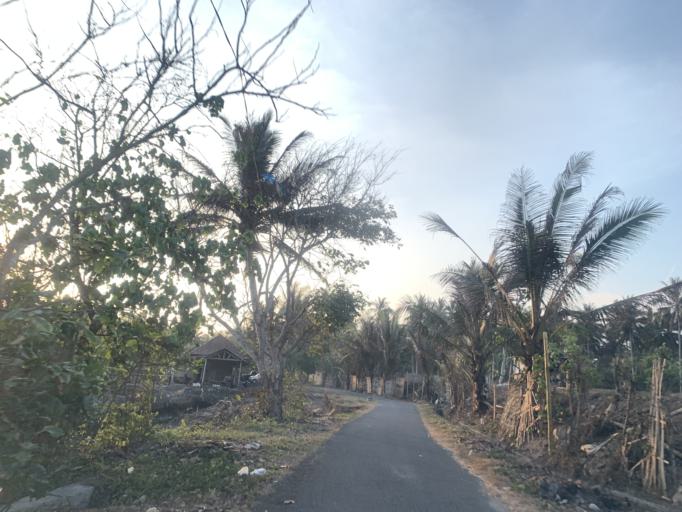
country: ID
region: Bali
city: Banjar Swastika
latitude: -8.4377
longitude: 114.8517
